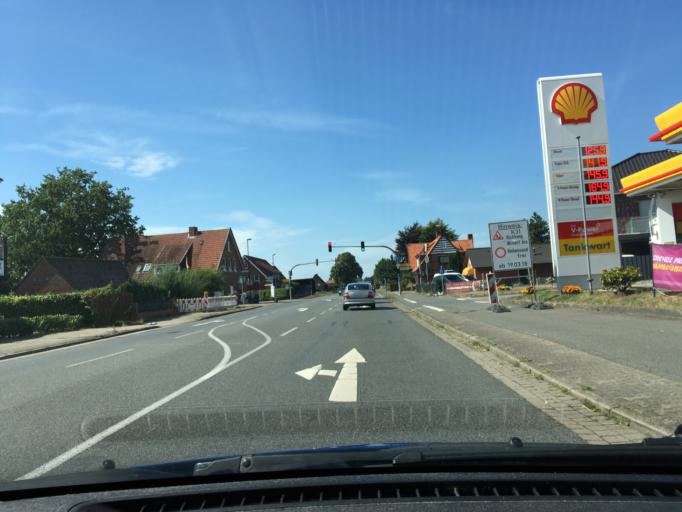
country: DE
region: Lower Saxony
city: Bardowick
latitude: 53.2917
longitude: 10.3886
